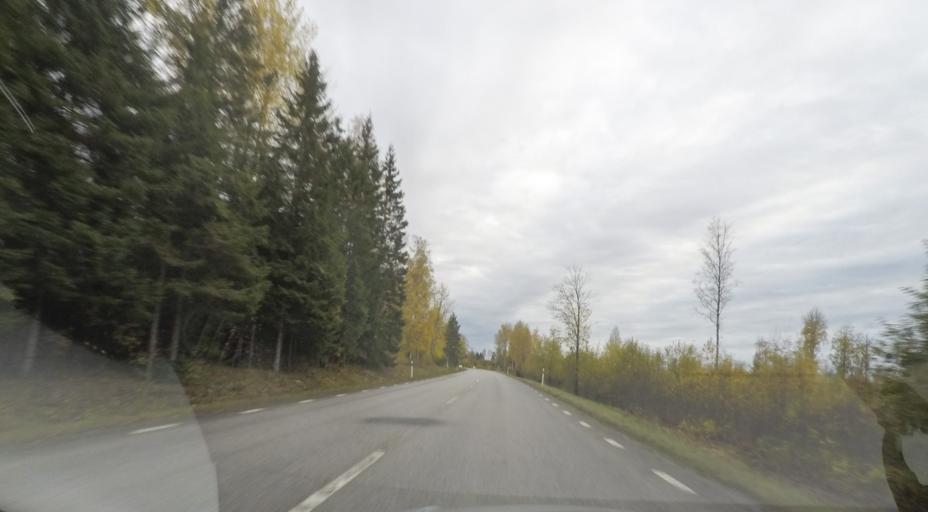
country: SE
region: OErebro
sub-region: Hallefors Kommun
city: Haellefors
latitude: 59.7216
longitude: 14.5244
